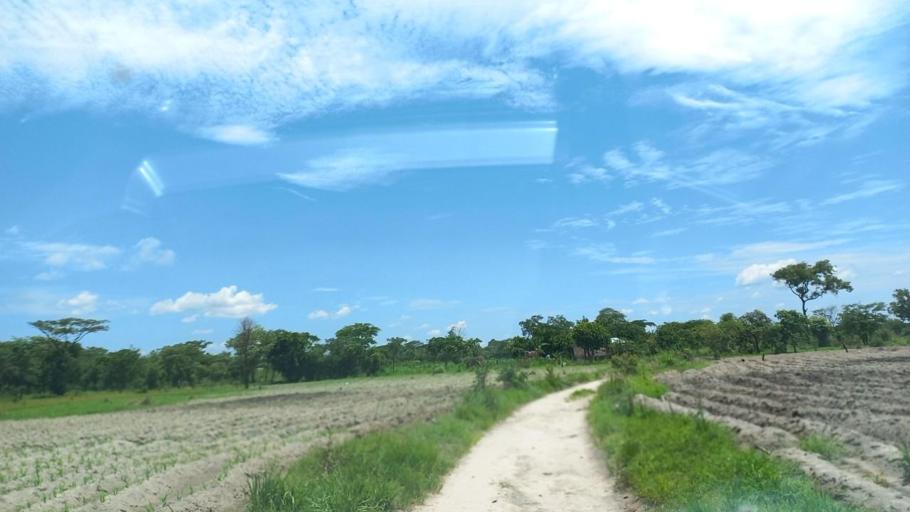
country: ZM
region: Copperbelt
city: Ndola
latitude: -12.8706
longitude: 28.4440
